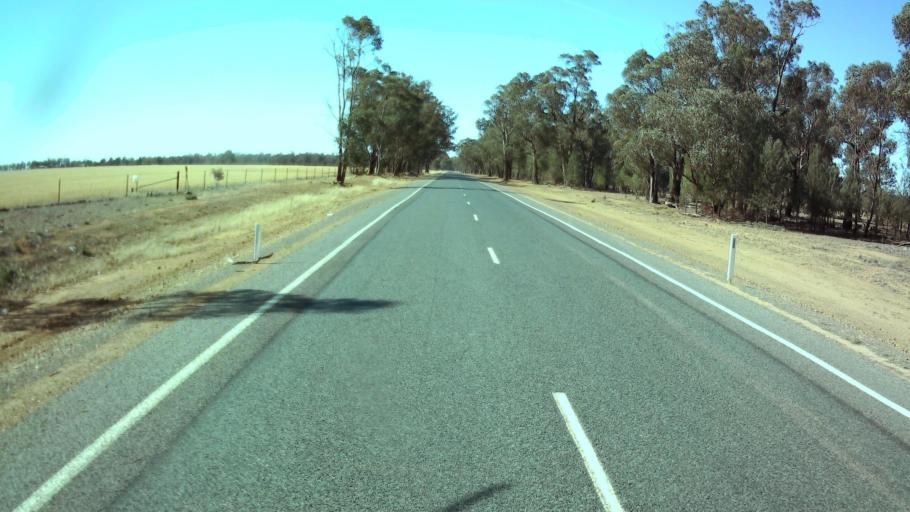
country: AU
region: New South Wales
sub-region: Weddin
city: Grenfell
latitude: -33.7401
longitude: 148.0887
